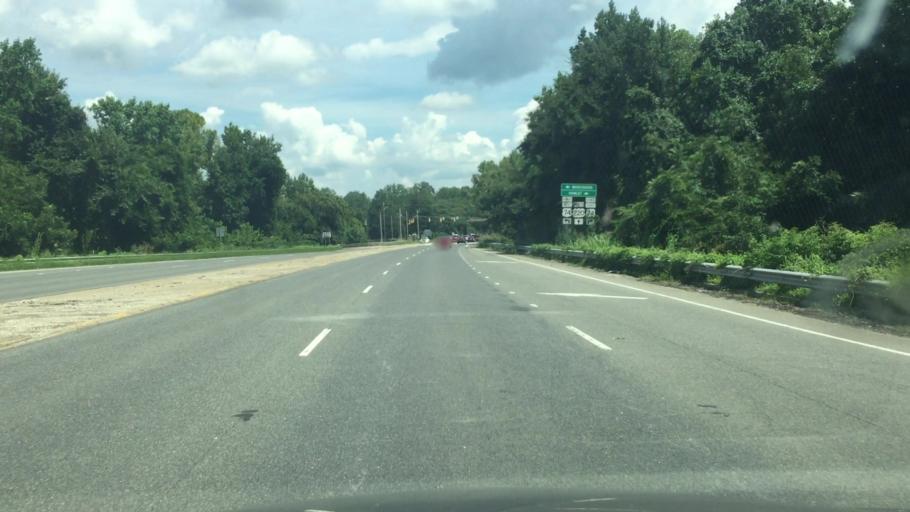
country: US
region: North Carolina
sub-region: Richmond County
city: Rockingham
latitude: 34.9354
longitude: -79.7801
